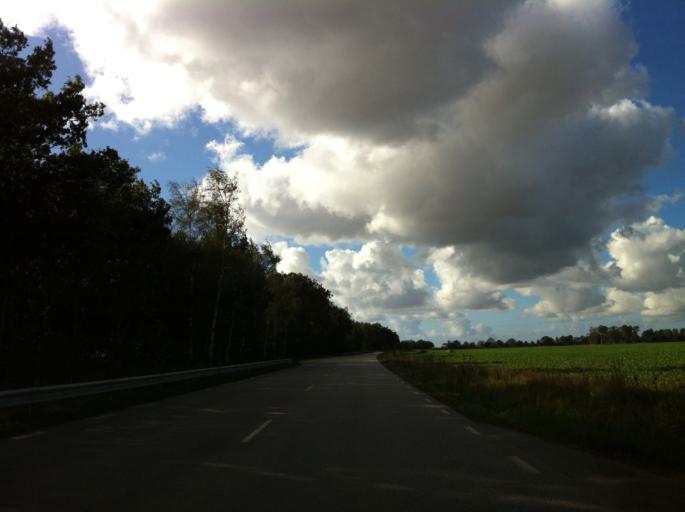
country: SE
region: Skane
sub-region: Eslovs Kommun
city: Eslov
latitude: 55.7900
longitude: 13.2324
